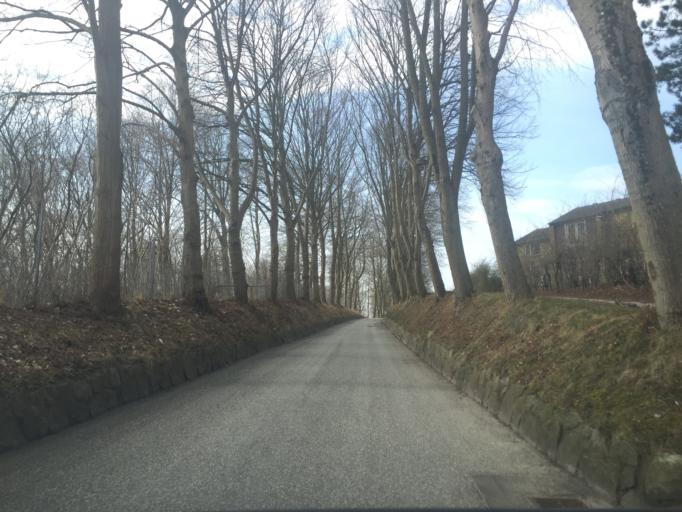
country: DK
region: Capital Region
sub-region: Lyngby-Tarbaek Kommune
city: Kongens Lyngby
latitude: 55.7942
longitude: 12.4973
